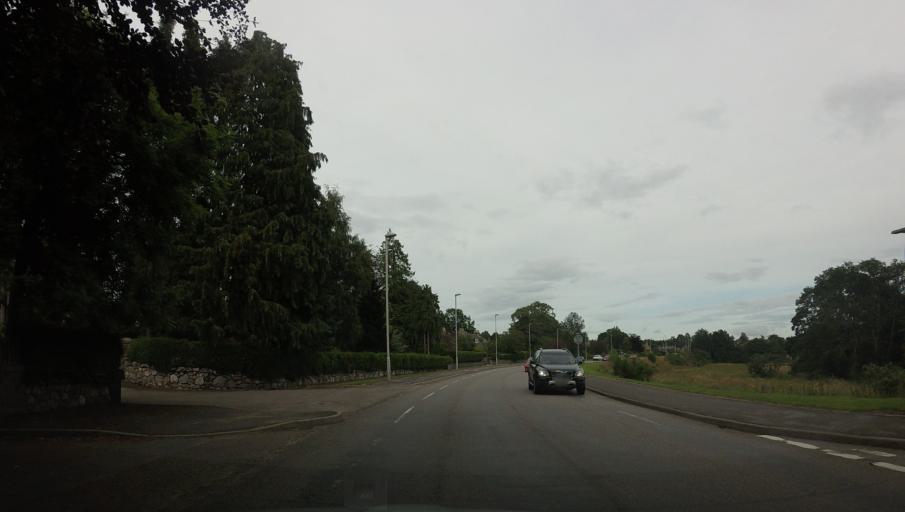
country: GB
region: Scotland
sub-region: Aberdeenshire
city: Aboyne
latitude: 57.0781
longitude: -2.7757
